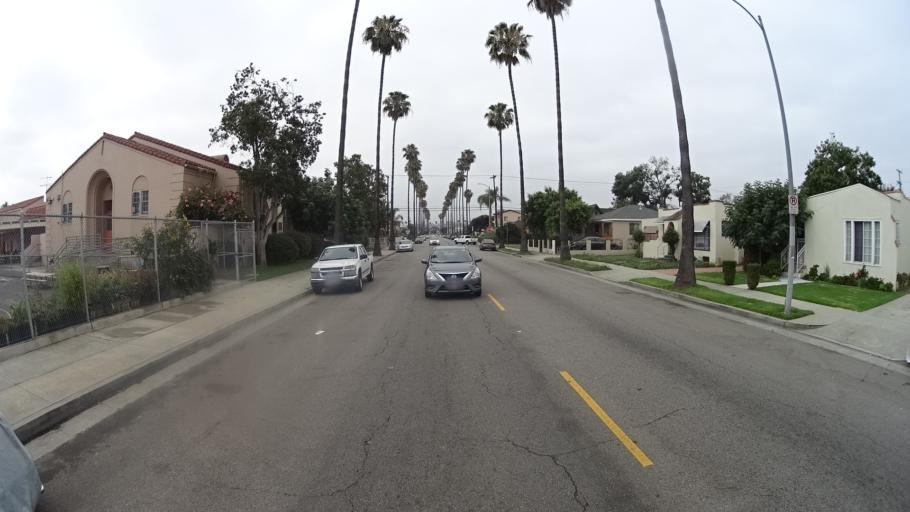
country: US
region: California
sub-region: Los Angeles County
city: View Park-Windsor Hills
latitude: 34.0282
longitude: -118.3405
